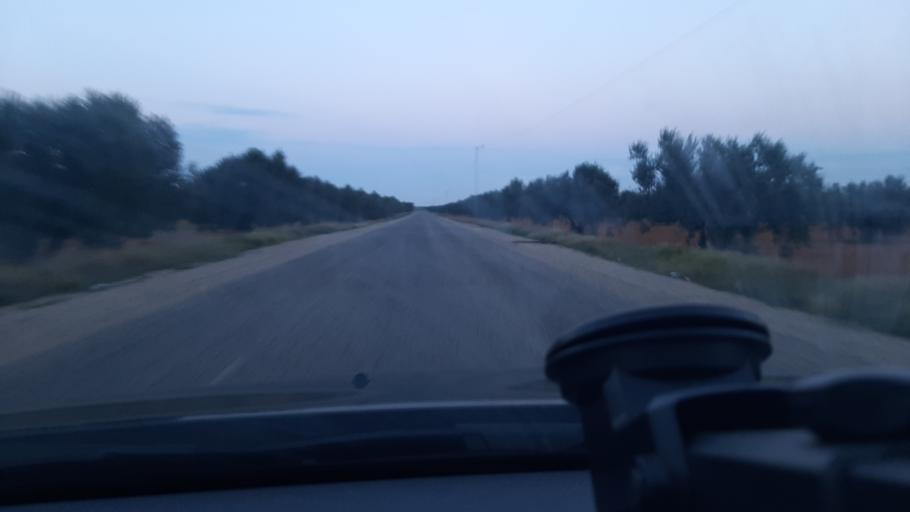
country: TN
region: Al Mahdiyah
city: Shurban
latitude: 35.0245
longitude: 10.4724
